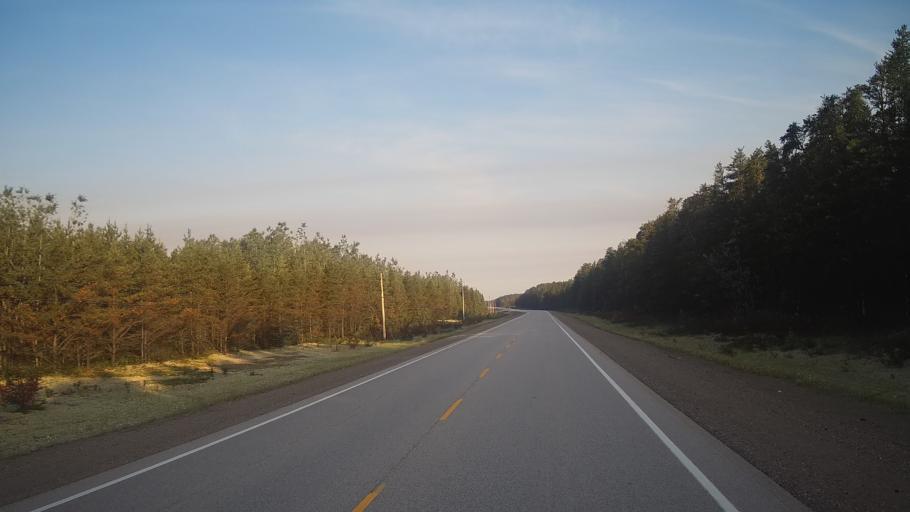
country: CA
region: Ontario
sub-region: Rainy River District
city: Atikokan
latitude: 49.2453
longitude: -91.0310
